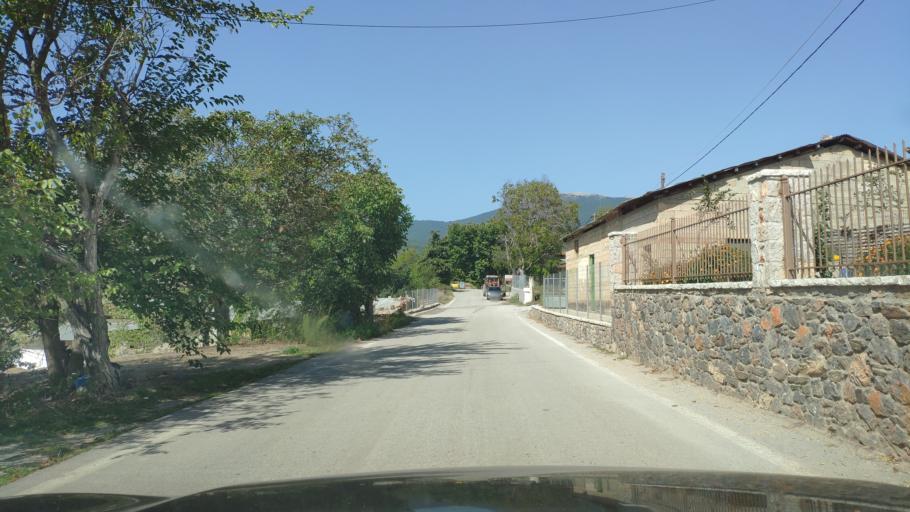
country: GR
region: West Greece
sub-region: Nomos Achaias
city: Aiyira
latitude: 37.9093
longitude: 22.3315
